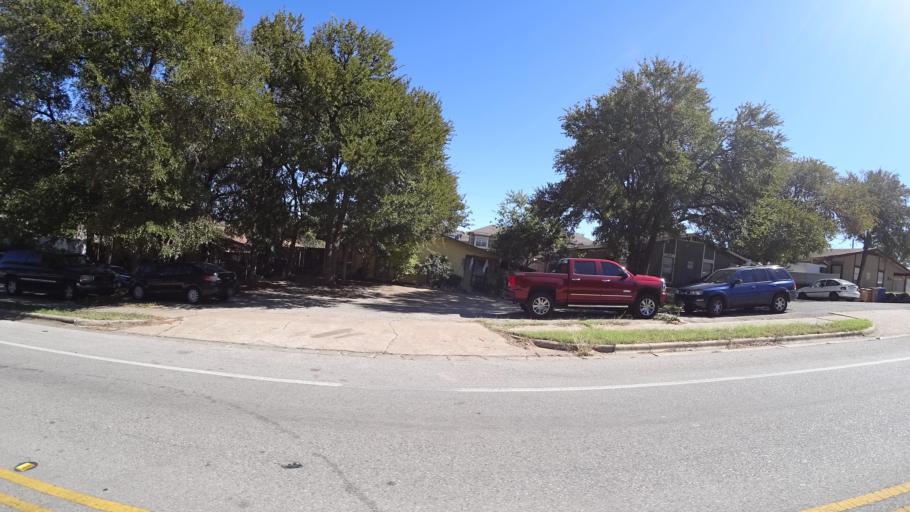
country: US
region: Texas
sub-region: Travis County
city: Austin
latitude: 30.2265
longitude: -97.7411
